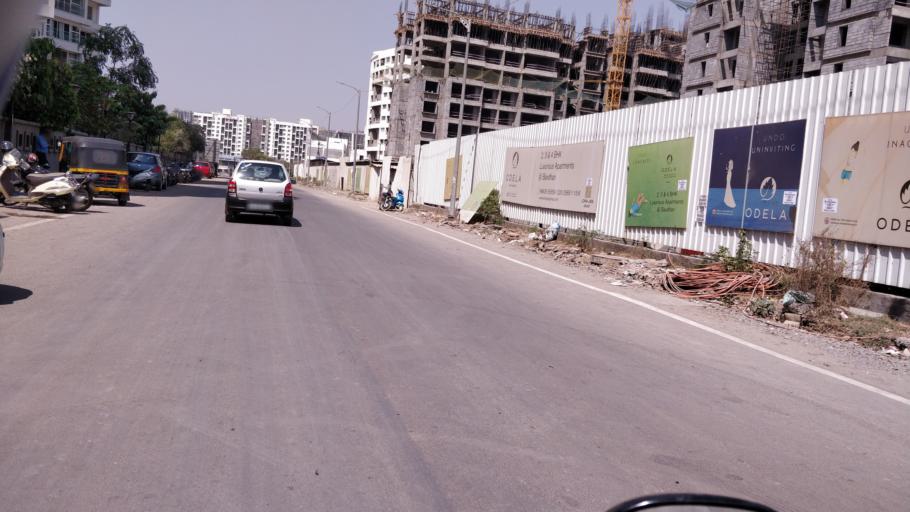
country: IN
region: Maharashtra
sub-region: Pune Division
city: Kharakvasla
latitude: 18.5115
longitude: 73.7743
